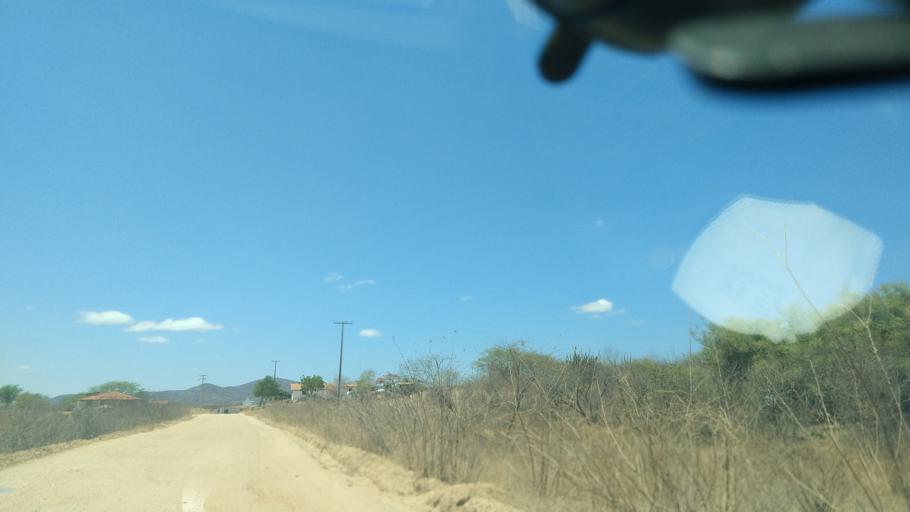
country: BR
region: Rio Grande do Norte
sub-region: Sao Tome
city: Sao Tome
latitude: -5.9788
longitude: -36.1732
